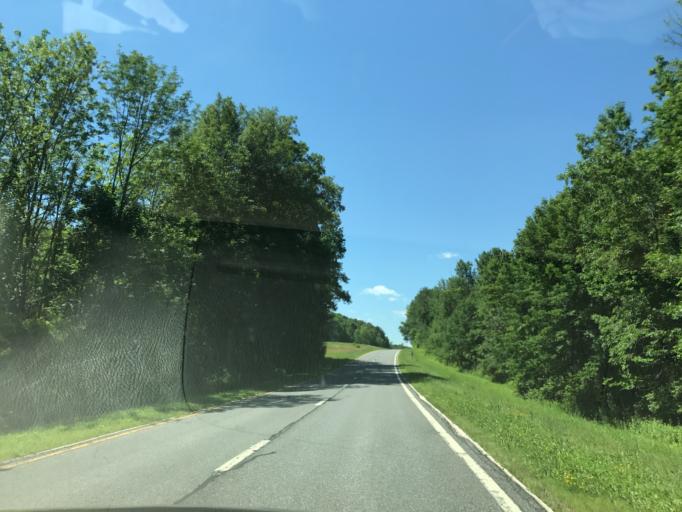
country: US
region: New York
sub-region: Dutchess County
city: Pine Plains
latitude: 41.9471
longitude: -73.7526
